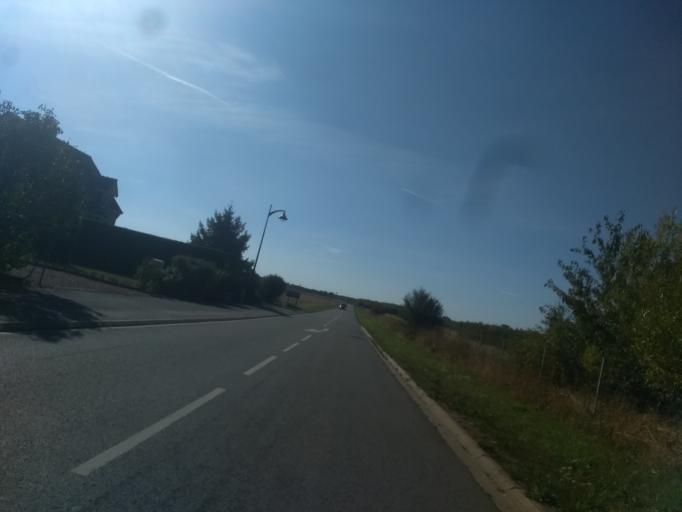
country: FR
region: Nord-Pas-de-Calais
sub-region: Departement du Pas-de-Calais
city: Roeux
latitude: 50.2732
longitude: 2.8860
